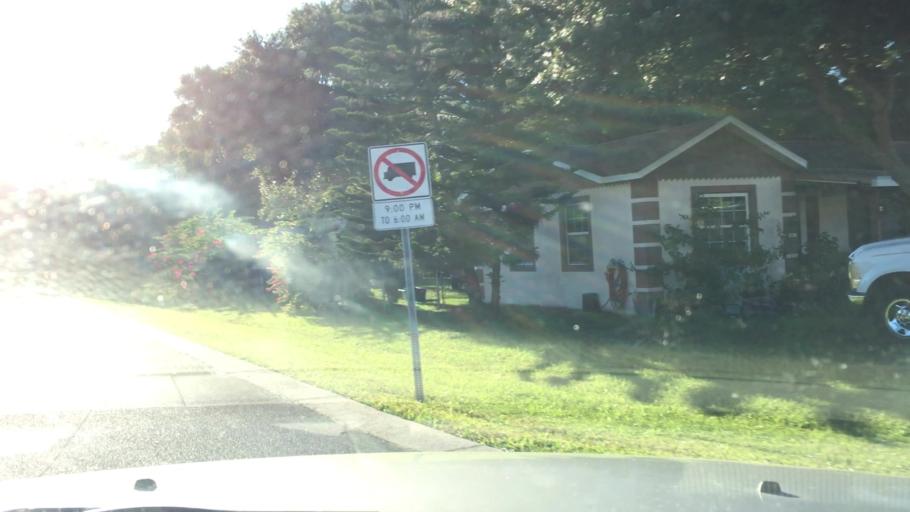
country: US
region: Florida
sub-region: Volusia County
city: Ormond Beach
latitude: 29.2625
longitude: -81.0520
